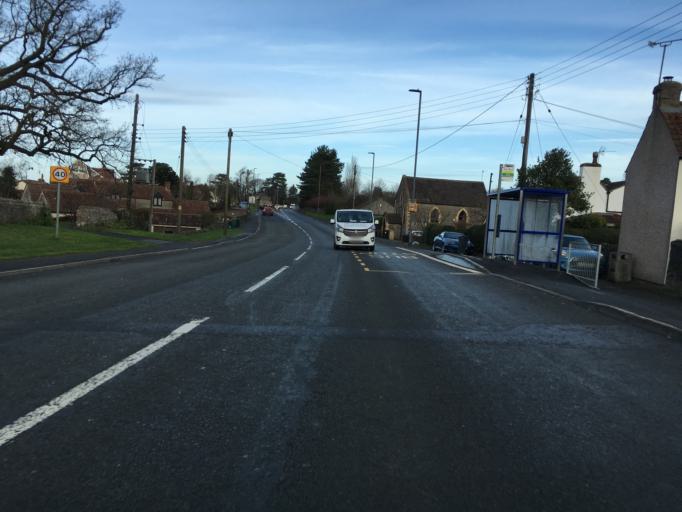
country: GB
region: England
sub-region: South Gloucestershire
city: Alveston
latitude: 51.5763
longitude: -2.5417
